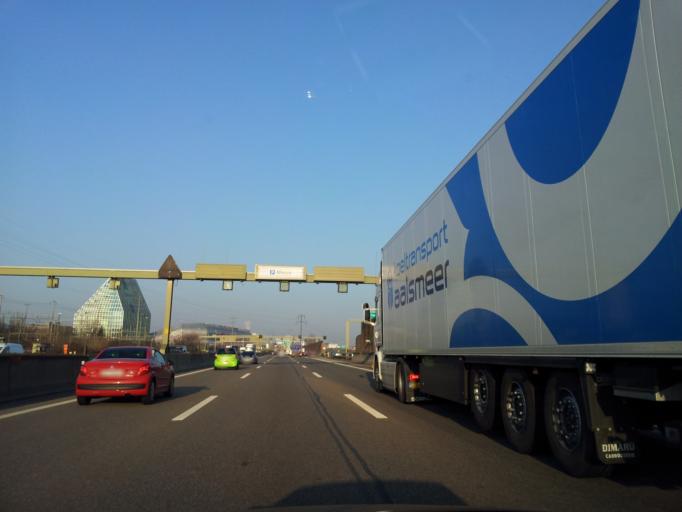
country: CH
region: Basel-Landschaft
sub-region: Bezirk Arlesheim
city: Birsfelden
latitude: 47.5416
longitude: 7.6286
